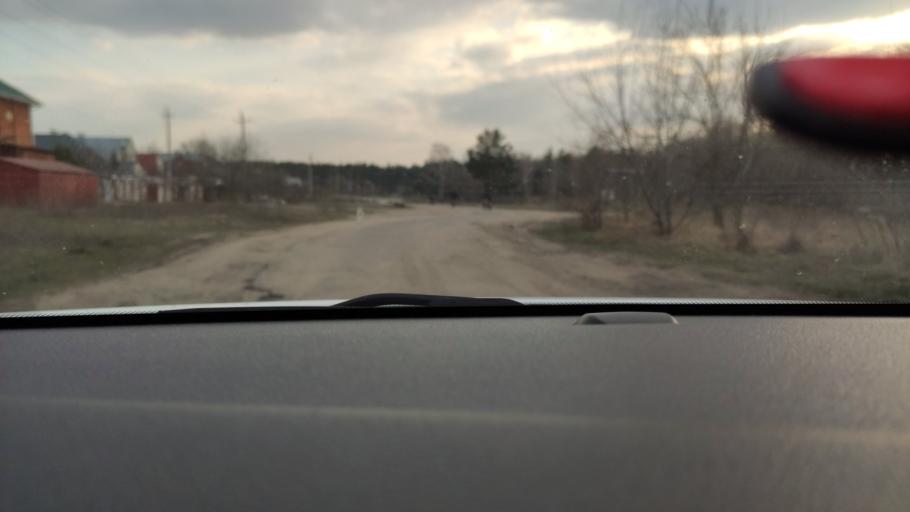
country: RU
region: Voronezj
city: Pridonskoy
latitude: 51.6367
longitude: 39.0891
